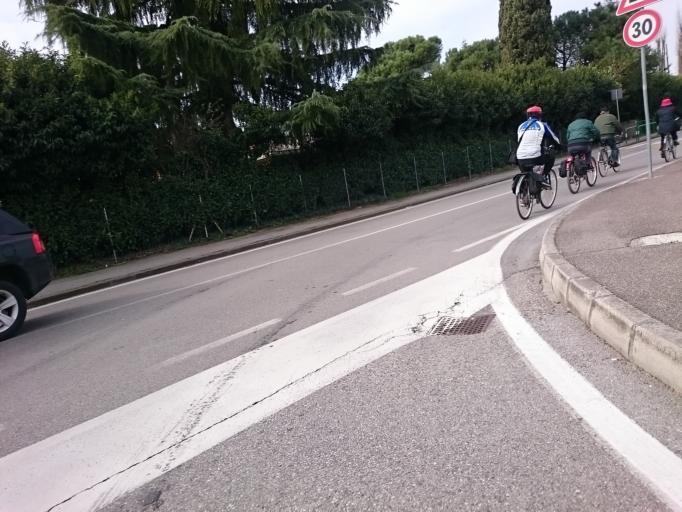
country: IT
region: Veneto
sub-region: Provincia di Padova
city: Mandriola-Sant'Agostino
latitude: 45.3494
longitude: 11.8640
